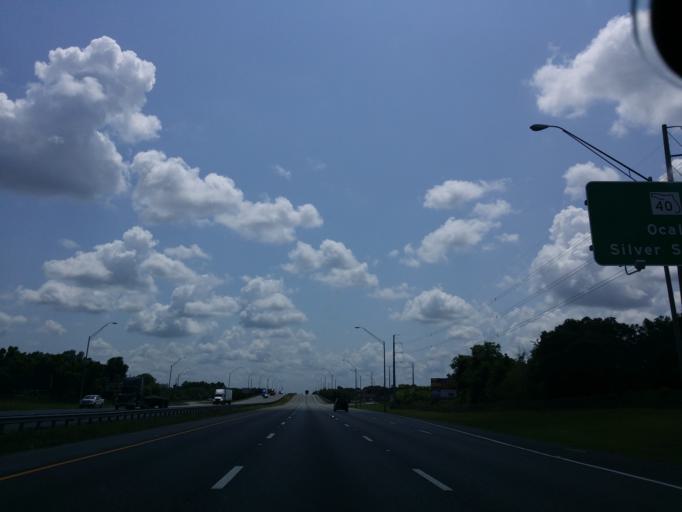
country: US
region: Florida
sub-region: Marion County
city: Ocala
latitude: 29.1917
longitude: -82.1848
